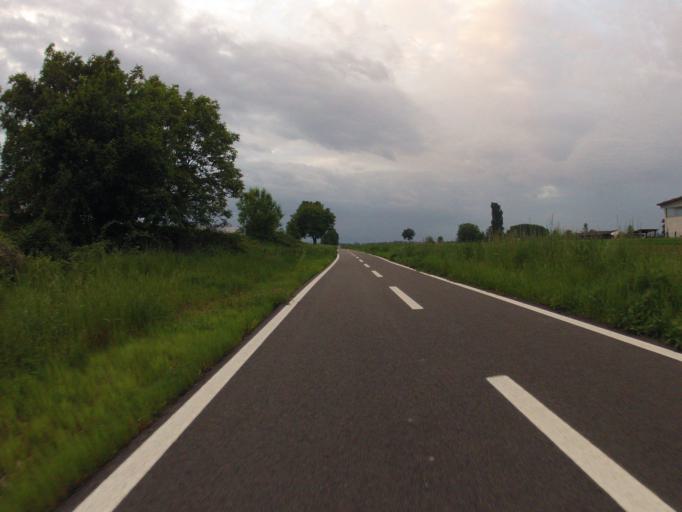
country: IT
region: Piedmont
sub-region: Provincia di Torino
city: Villafranca Piemonte
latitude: 44.7881
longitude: 7.5094
